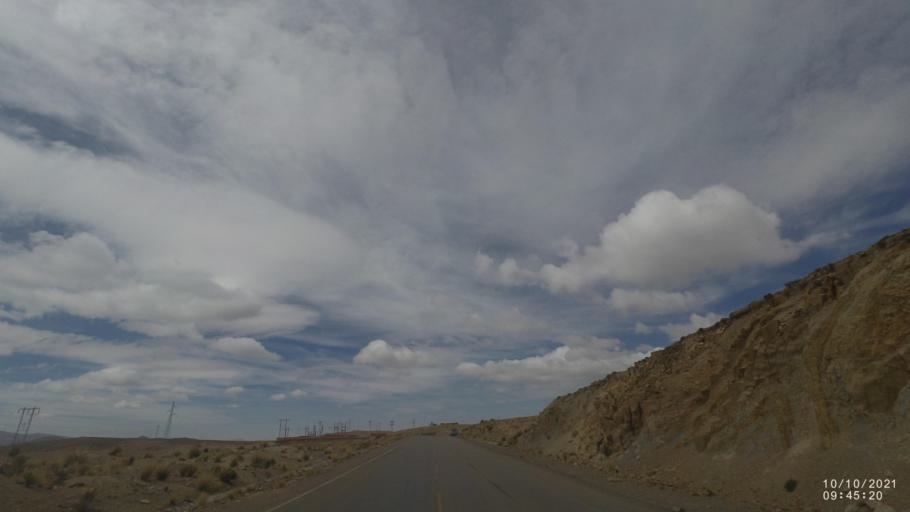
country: BO
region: La Paz
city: Quime
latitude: -17.1700
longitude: -67.3355
